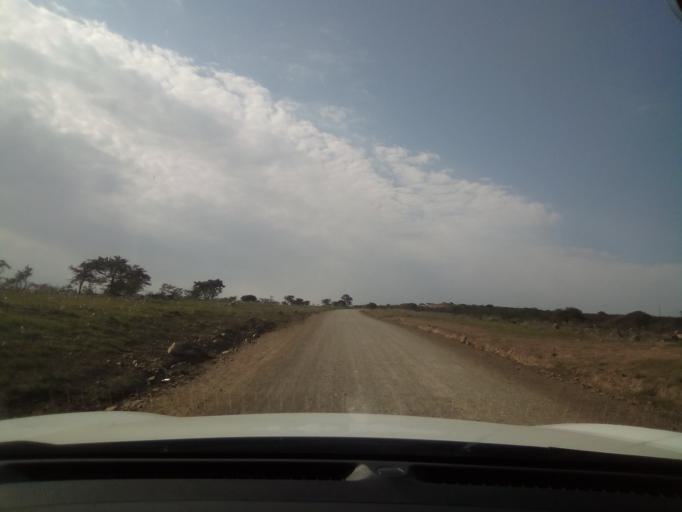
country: ZA
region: Eastern Cape
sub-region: Buffalo City Metropolitan Municipality
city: Bhisho
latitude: -32.9876
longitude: 27.2462
